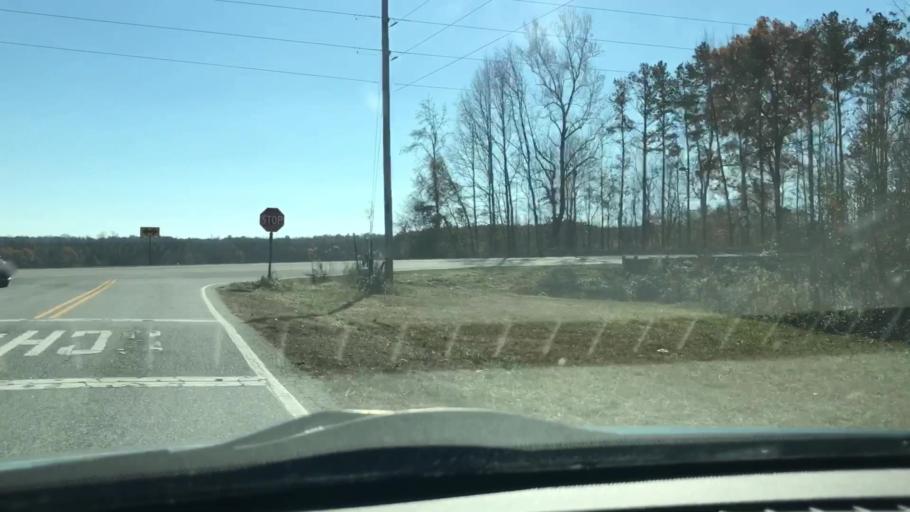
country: US
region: North Carolina
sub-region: Davidson County
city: Denton
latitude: 35.6400
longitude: -79.9720
